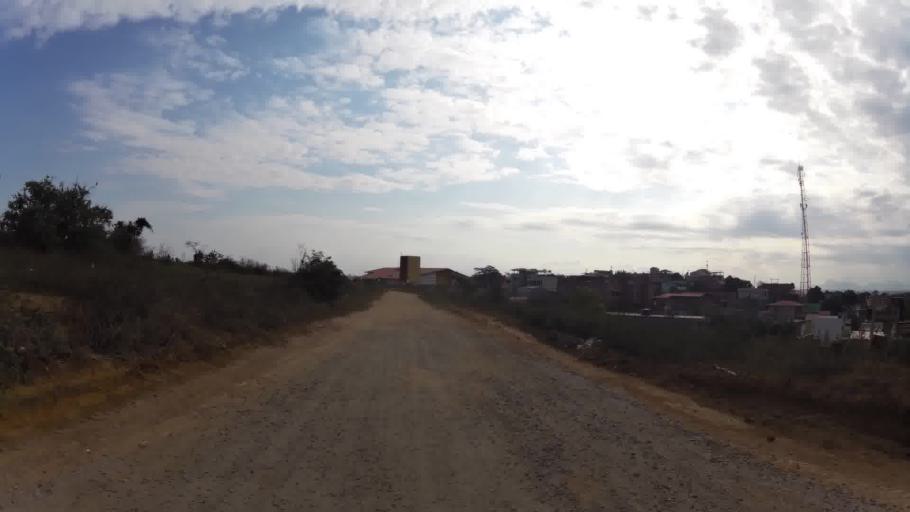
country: BR
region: Espirito Santo
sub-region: Itapemirim
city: Itapemirim
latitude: -21.0126
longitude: -40.8287
